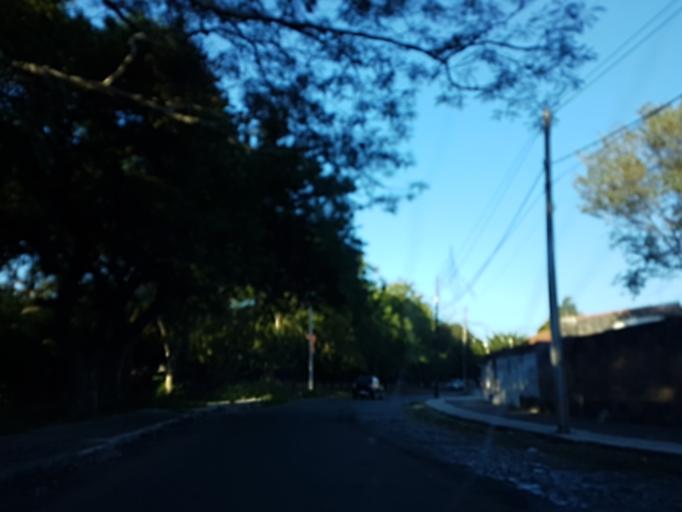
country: PY
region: Asuncion
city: Asuncion
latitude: -25.2684
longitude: -57.5958
